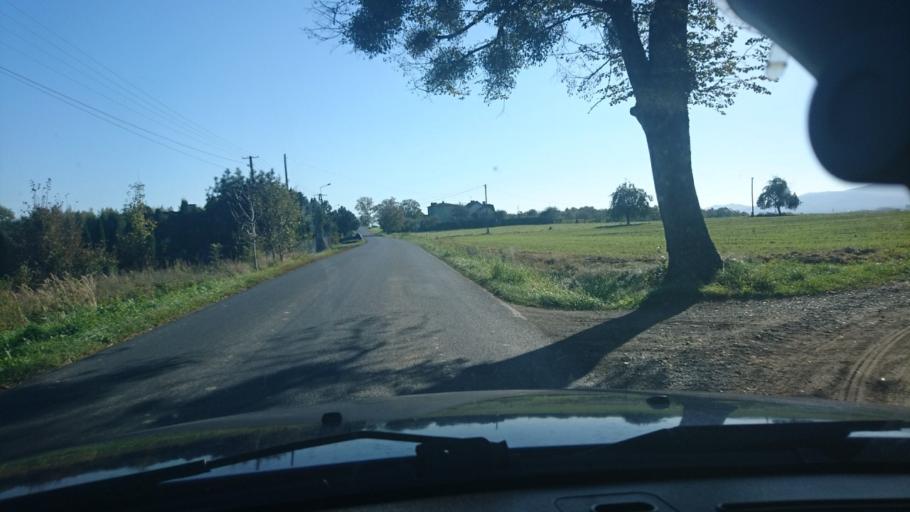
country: PL
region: Silesian Voivodeship
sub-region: Powiat bielski
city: Bronow
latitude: 49.8581
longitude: 18.9063
